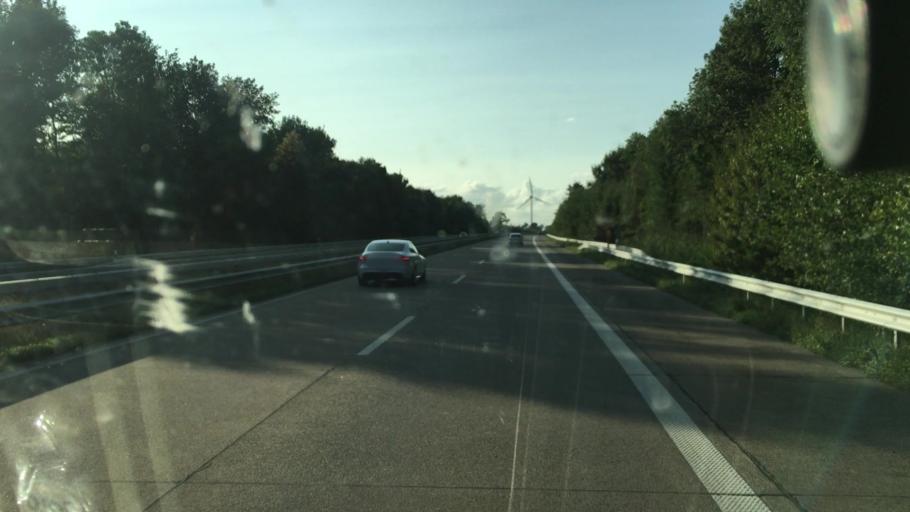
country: DE
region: Lower Saxony
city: Bockhorn
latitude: 53.4320
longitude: 8.0496
